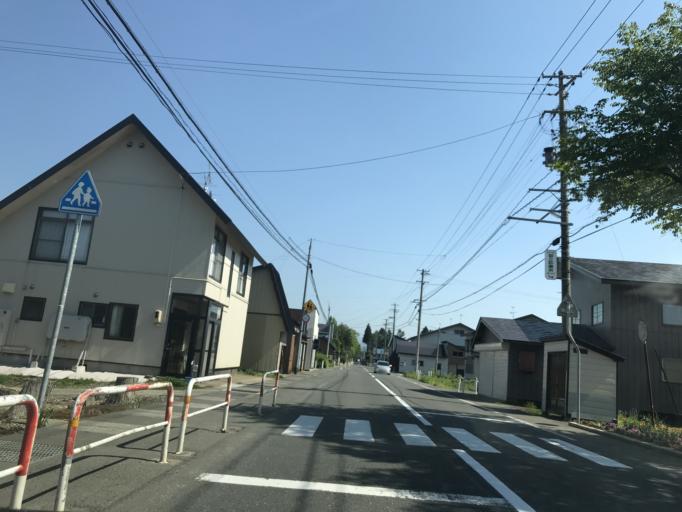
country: JP
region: Akita
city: Yokotemachi
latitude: 39.3981
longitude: 140.7568
